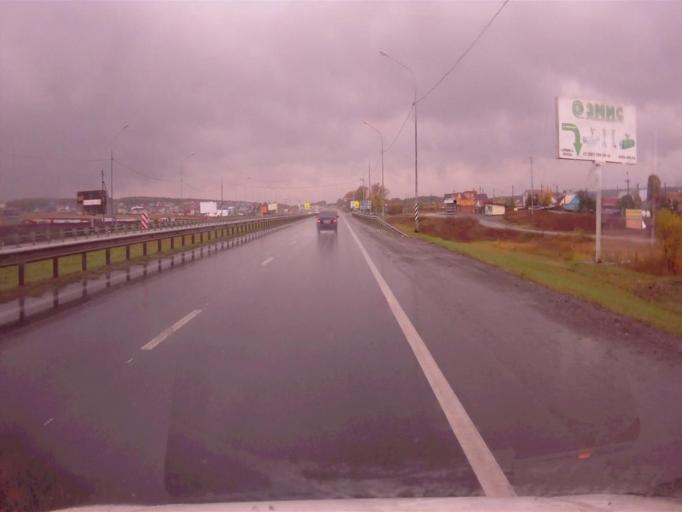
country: RU
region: Chelyabinsk
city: Dolgoderevenskoye
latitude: 55.2719
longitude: 61.3440
